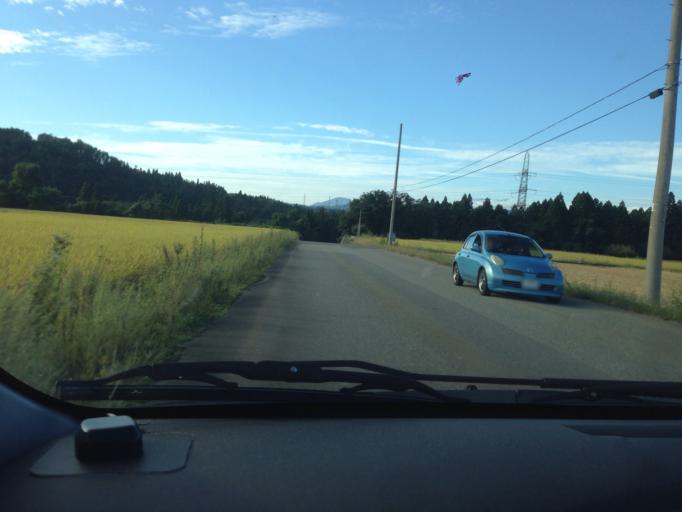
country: JP
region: Fukushima
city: Kitakata
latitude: 37.5930
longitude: 139.7634
